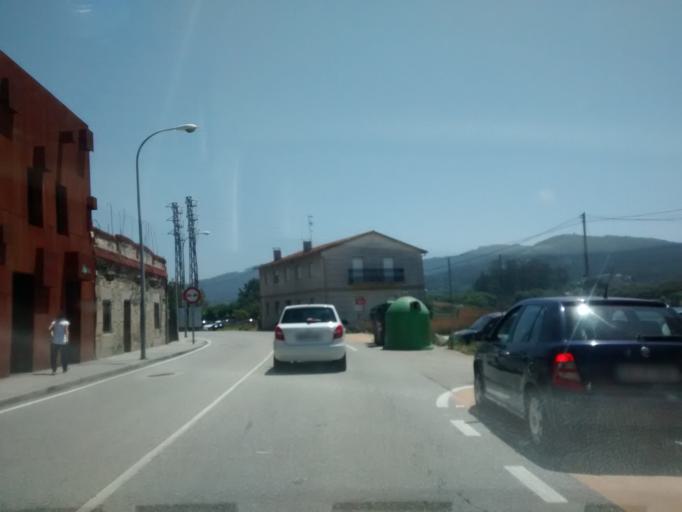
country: ES
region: Galicia
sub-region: Provincia de Pontevedra
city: Nigran
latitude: 42.1155
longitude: -8.8110
